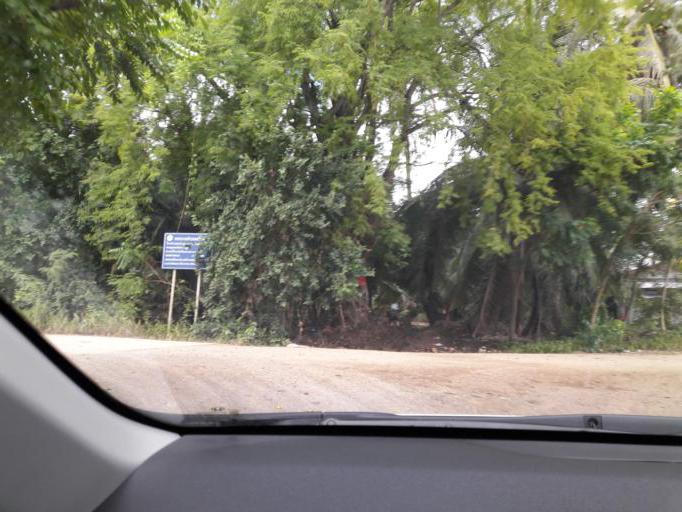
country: TH
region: Ratchaburi
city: Damnoen Saduak
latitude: 13.5443
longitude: 100.0096
